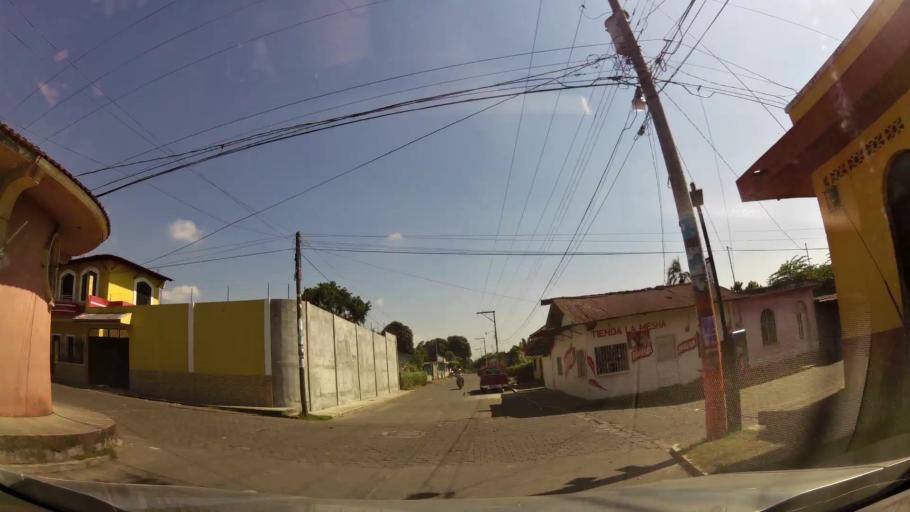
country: GT
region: Suchitepeque
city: Mazatenango
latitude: 14.5297
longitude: -91.4887
